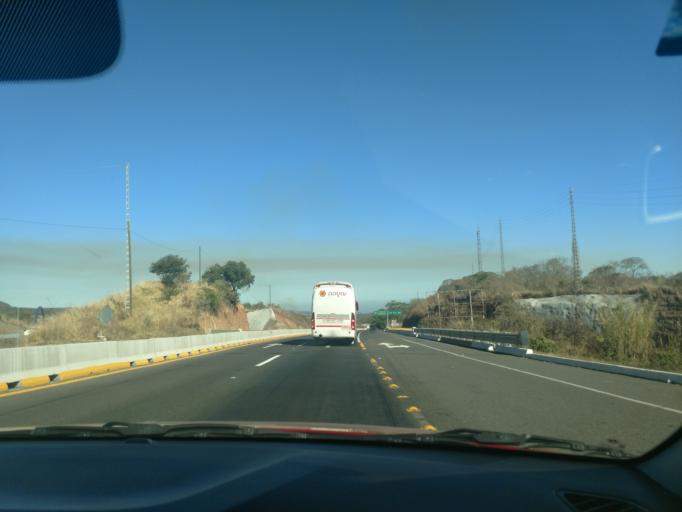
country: MX
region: Nayarit
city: Tepic
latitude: 21.5605
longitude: -104.9697
